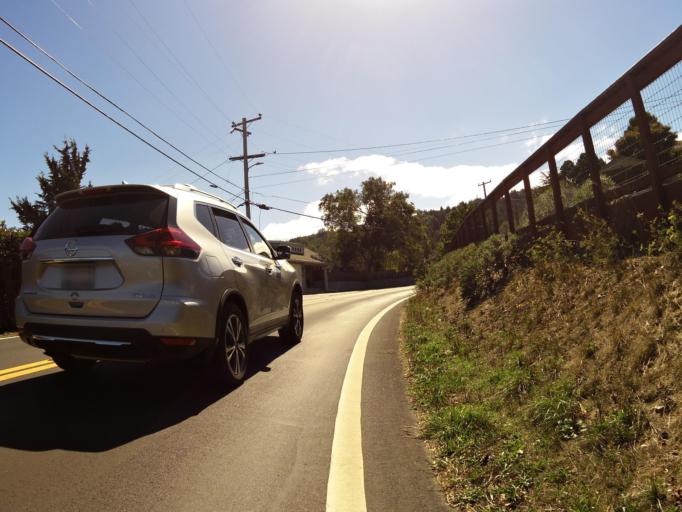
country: US
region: California
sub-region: Marin County
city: Corte Madera
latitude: 37.9245
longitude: -122.5292
